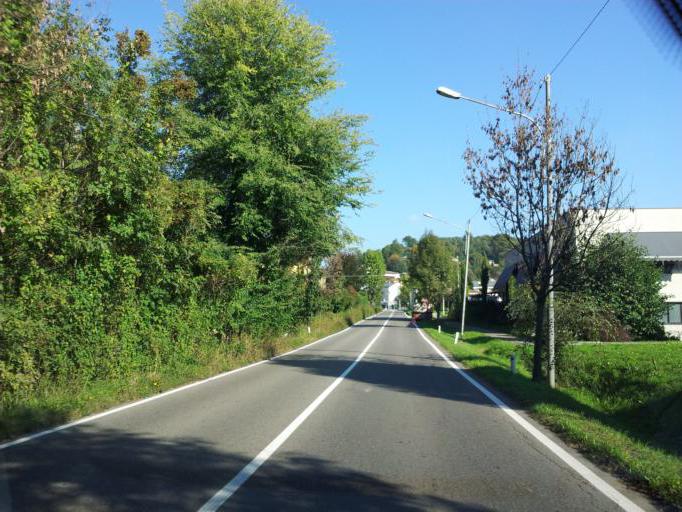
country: IT
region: Lombardy
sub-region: Provincia di Varese
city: Azzate
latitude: 45.7737
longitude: 8.7865
